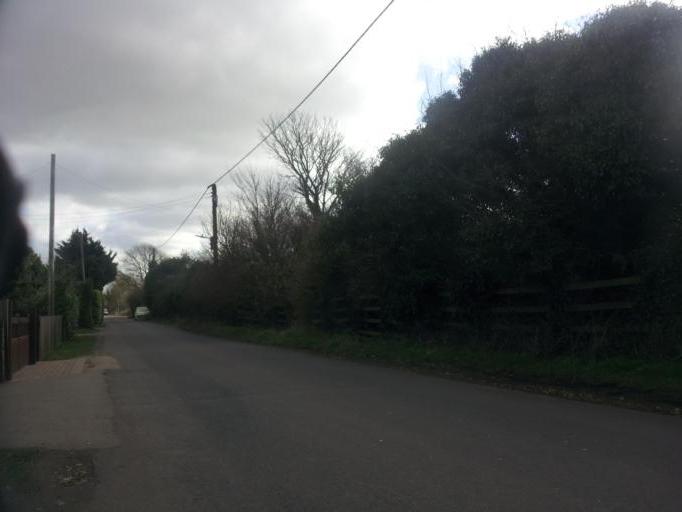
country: GB
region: England
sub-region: Kent
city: Aylesford
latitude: 51.3324
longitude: 0.4995
